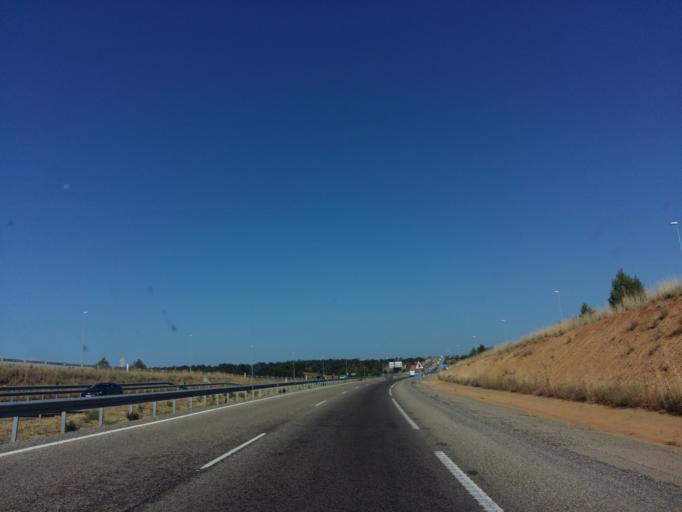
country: ES
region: Castille and Leon
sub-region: Provincia de Leon
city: Leon
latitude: 42.5676
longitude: -5.5975
